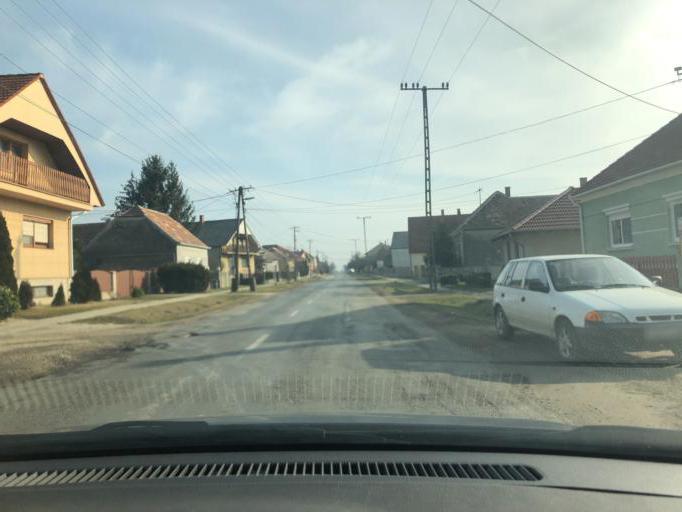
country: HU
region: Gyor-Moson-Sopron
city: Kapuvar
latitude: 47.5934
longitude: 17.0927
